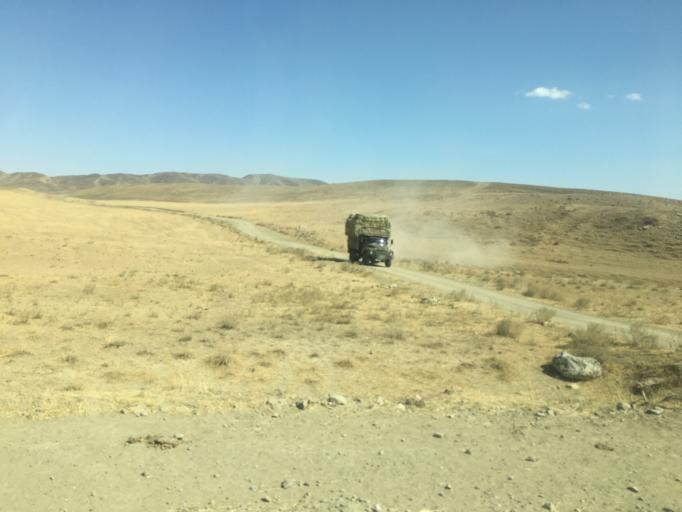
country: TM
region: Ahal
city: Baharly
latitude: 38.4244
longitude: 57.0223
